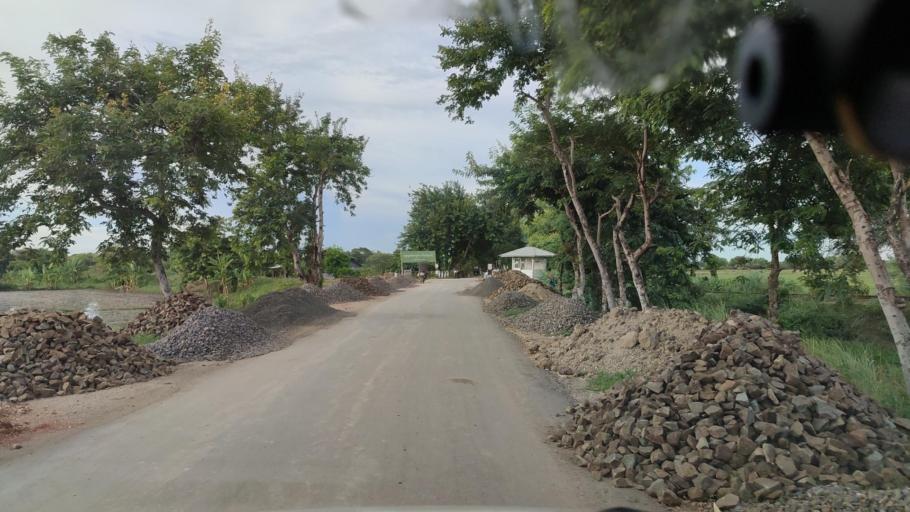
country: MM
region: Magway
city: Minbu
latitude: 20.3107
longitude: 94.7558
